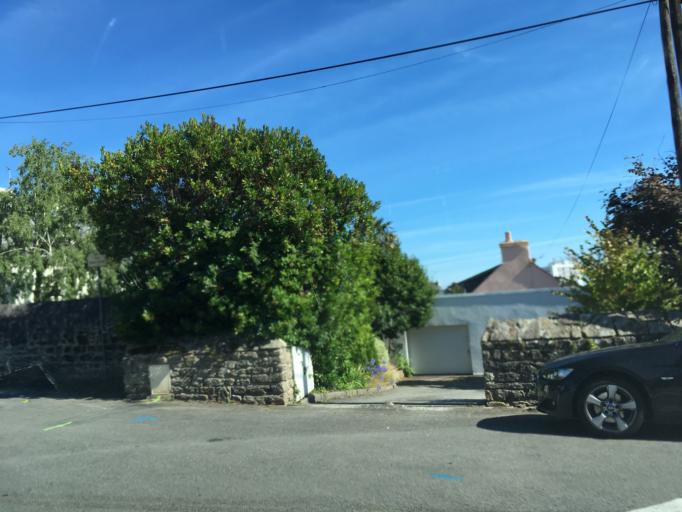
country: FR
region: Brittany
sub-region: Departement du Finistere
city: Quimper
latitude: 47.9852
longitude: -4.1044
